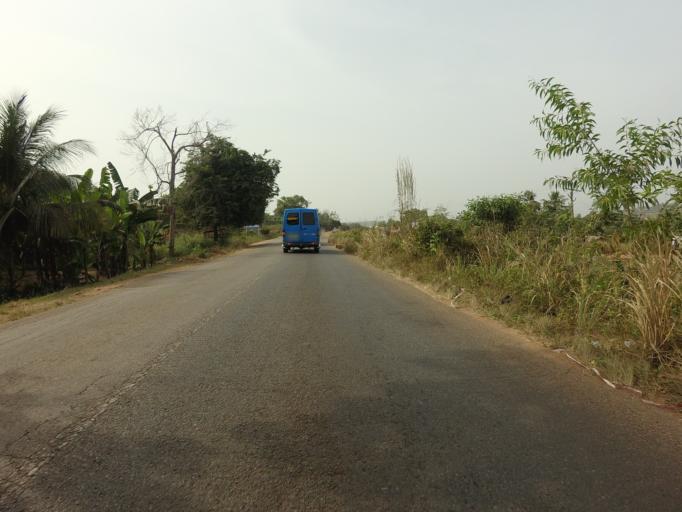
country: GH
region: Volta
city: Ho
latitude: 6.6034
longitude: 0.4521
